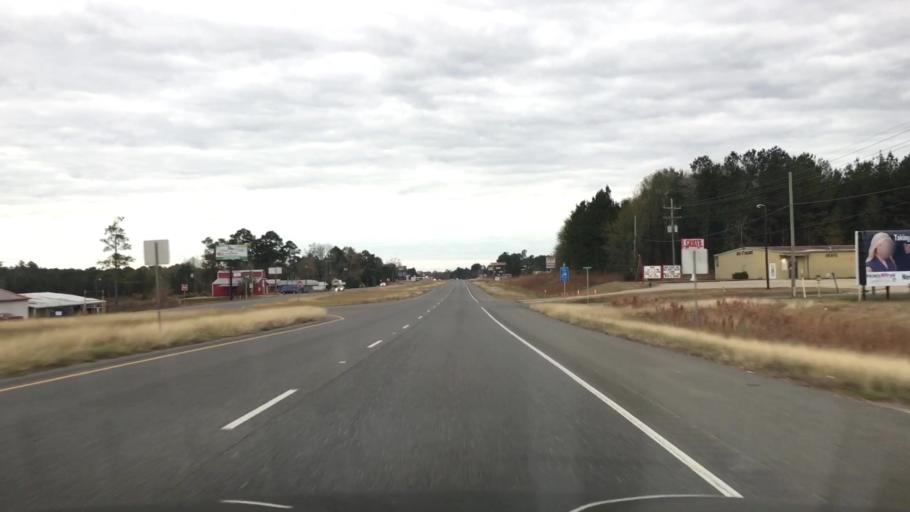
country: US
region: Louisiana
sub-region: Vernon Parish
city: New Llano
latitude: 31.0844
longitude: -93.2719
